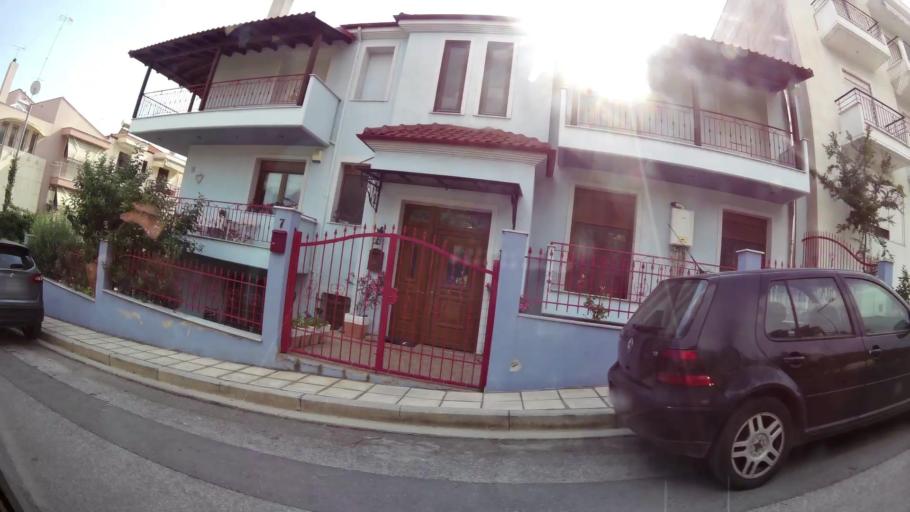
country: GR
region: Central Macedonia
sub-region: Nomos Thessalonikis
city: Polichni
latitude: 40.6620
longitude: 22.9545
